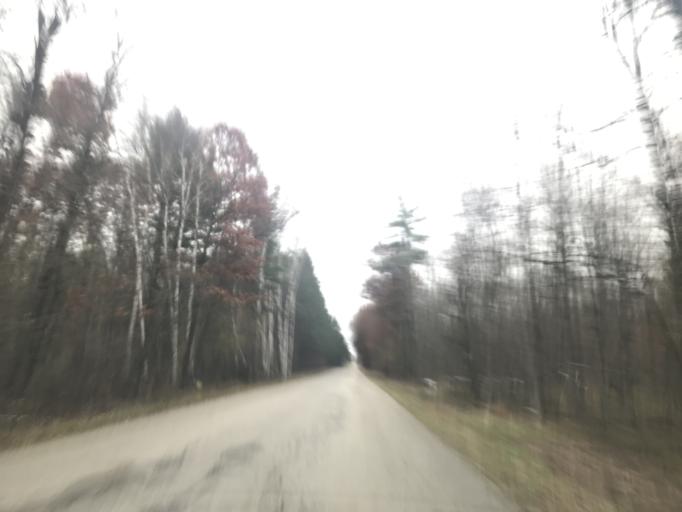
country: US
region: Wisconsin
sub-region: Marinette County
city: Peshtigo
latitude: 45.1173
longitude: -87.7499
